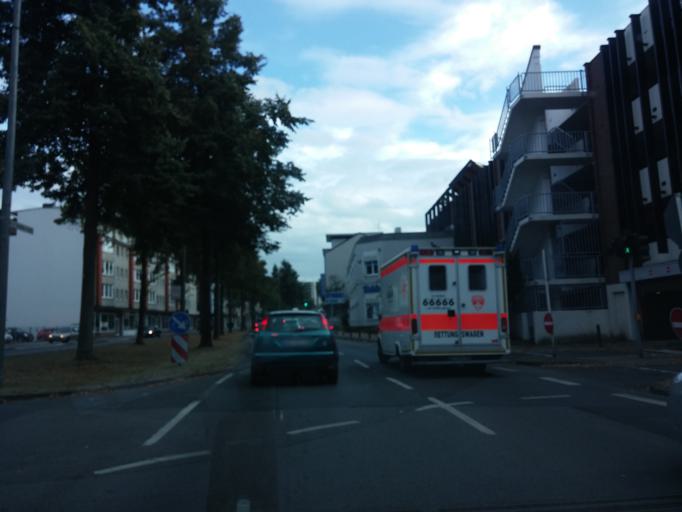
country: DE
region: North Rhine-Westphalia
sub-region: Regierungsbezirk Munster
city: Gladbeck
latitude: 51.5803
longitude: 7.0542
